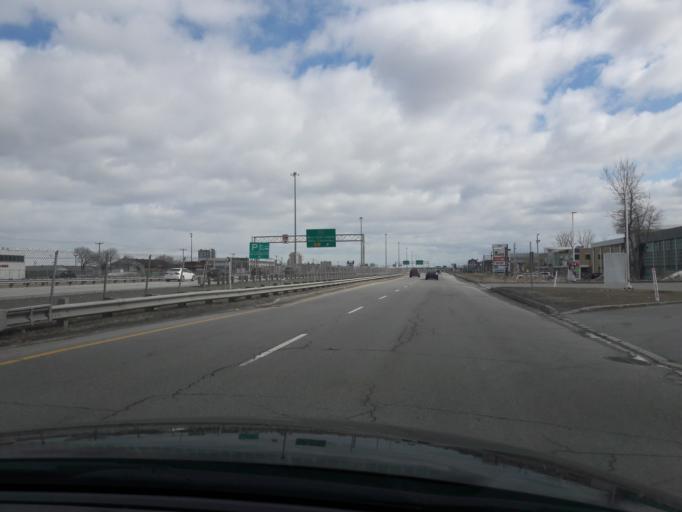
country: CA
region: Quebec
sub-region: Laurentides
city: Boisbriand
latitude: 45.5596
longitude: -73.7908
